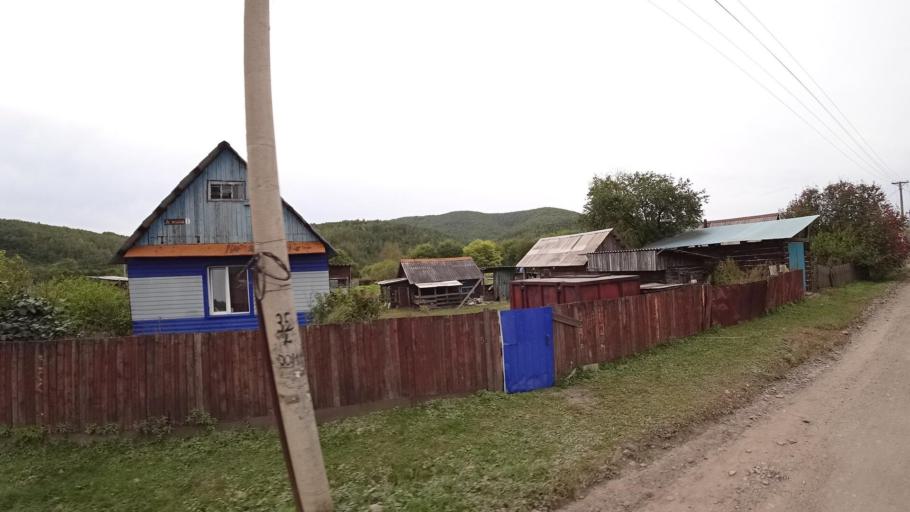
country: RU
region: Jewish Autonomous Oblast
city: Khingansk
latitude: 49.0323
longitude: 131.0492
